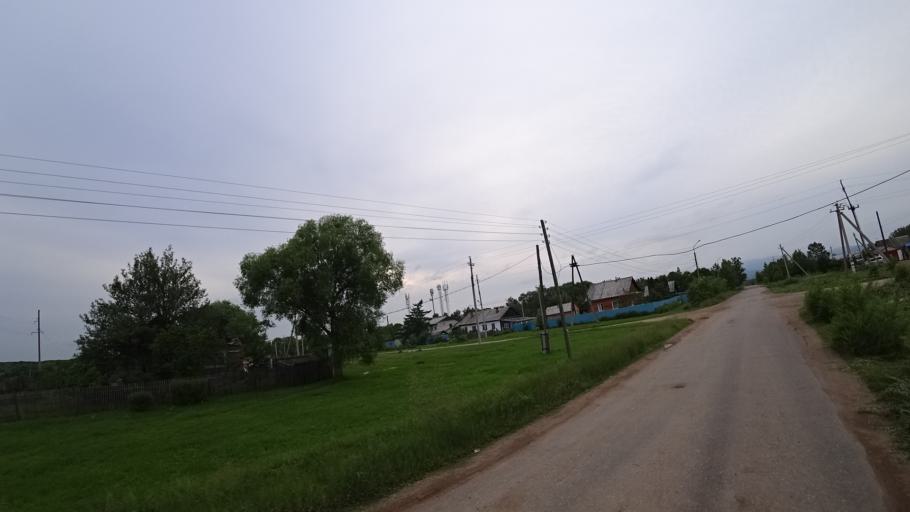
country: RU
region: Primorskiy
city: Novosysoyevka
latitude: 44.2320
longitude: 133.3602
